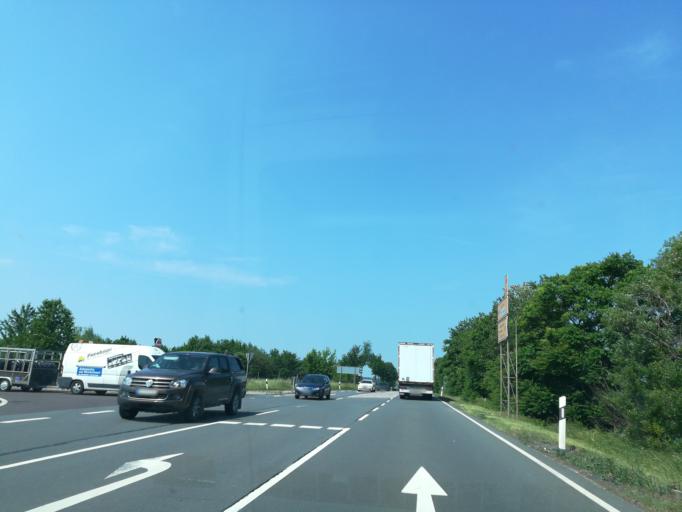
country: DE
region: Saxony-Anhalt
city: Aschersleben
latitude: 51.7834
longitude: 11.4582
